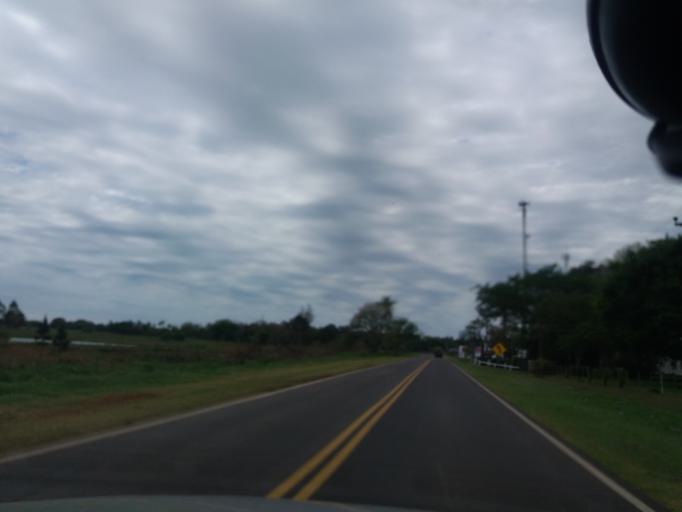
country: AR
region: Corrientes
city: Riachuelo
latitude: -27.4574
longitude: -58.7099
